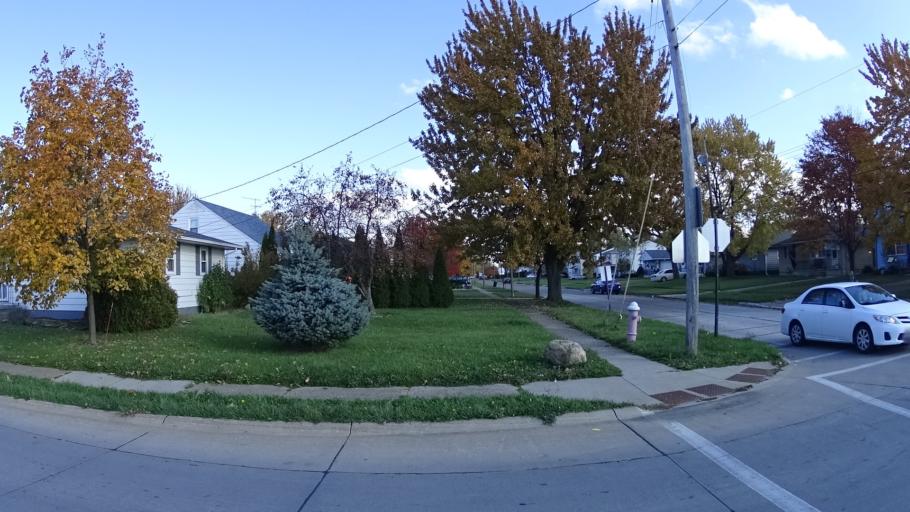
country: US
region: Ohio
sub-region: Lorain County
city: Lorain
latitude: 41.4483
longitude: -82.1888
